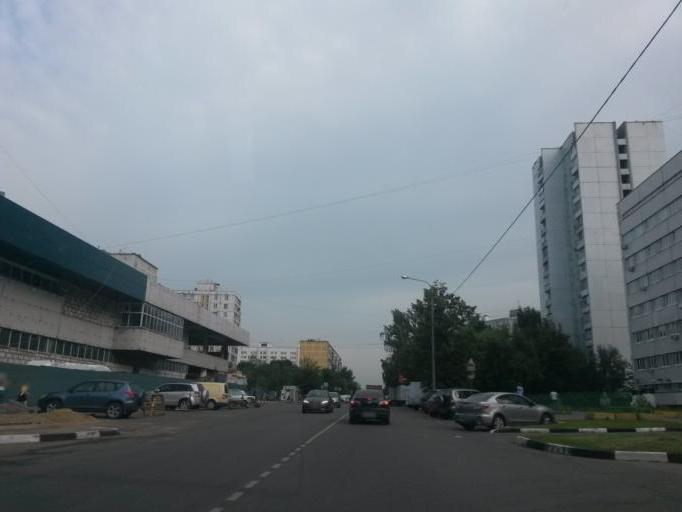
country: RU
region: Moscow
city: Orekhovo-Borisovo
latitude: 55.6077
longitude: 37.7330
